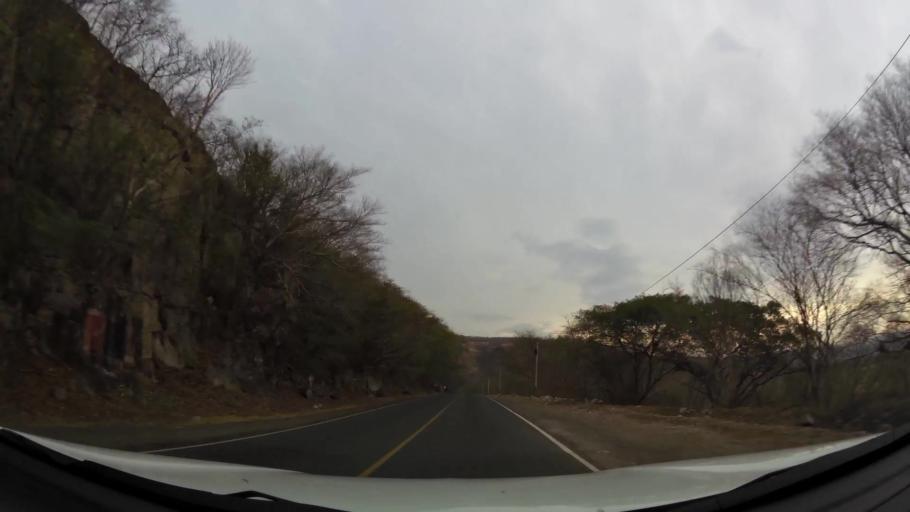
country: NI
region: Leon
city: La Jicaral
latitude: 12.6764
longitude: -86.4269
